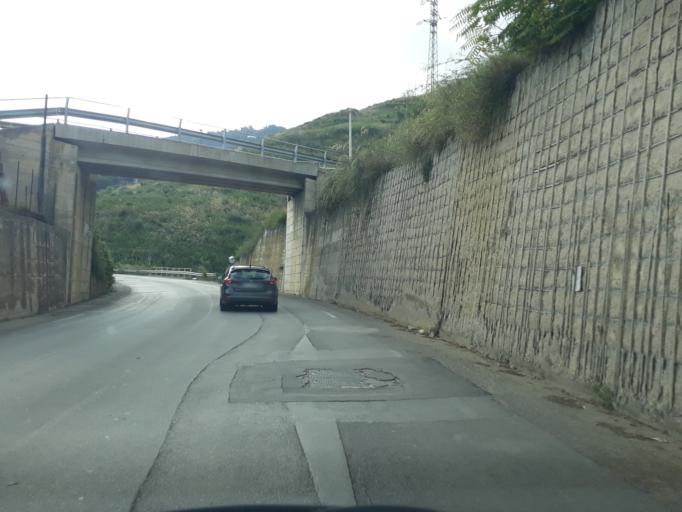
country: IT
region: Sicily
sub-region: Palermo
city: Cefalu
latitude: 38.0283
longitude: 14.0060
